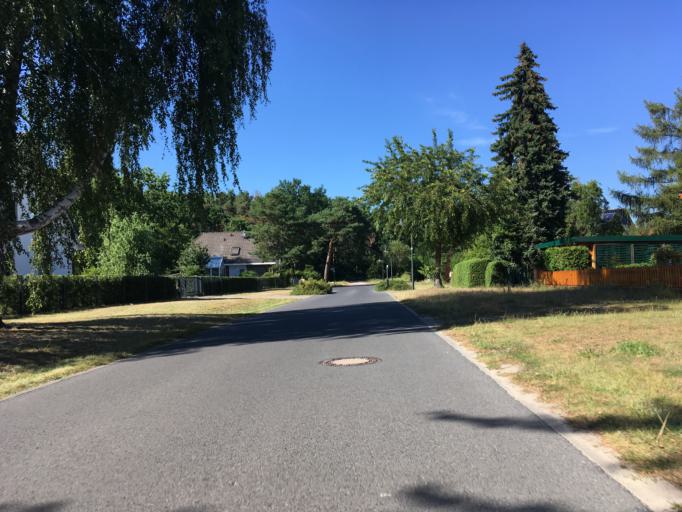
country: DE
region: Brandenburg
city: Schulzendorf
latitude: 52.3747
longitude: 13.5930
